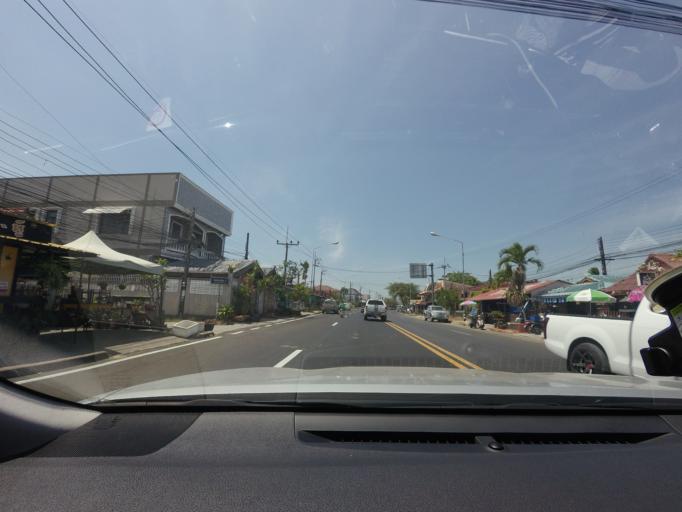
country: TH
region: Narathiwat
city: Narathiwat
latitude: 6.4447
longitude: 101.8134
